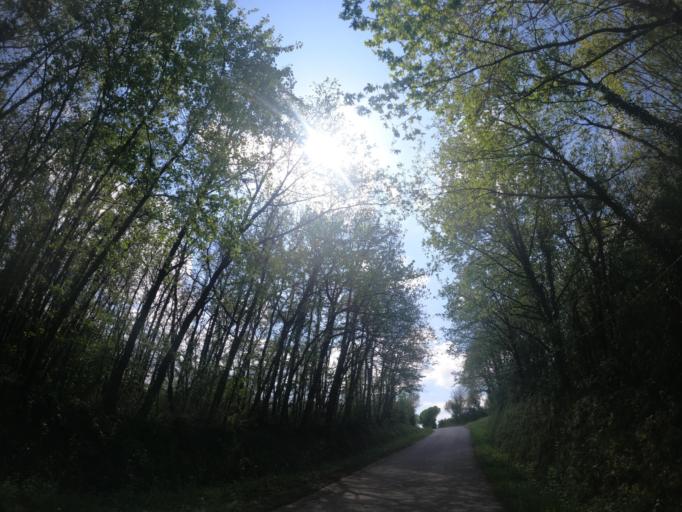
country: FR
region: Poitou-Charentes
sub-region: Departement des Deux-Sevres
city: Saint-Varent
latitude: 46.8517
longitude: -0.2737
